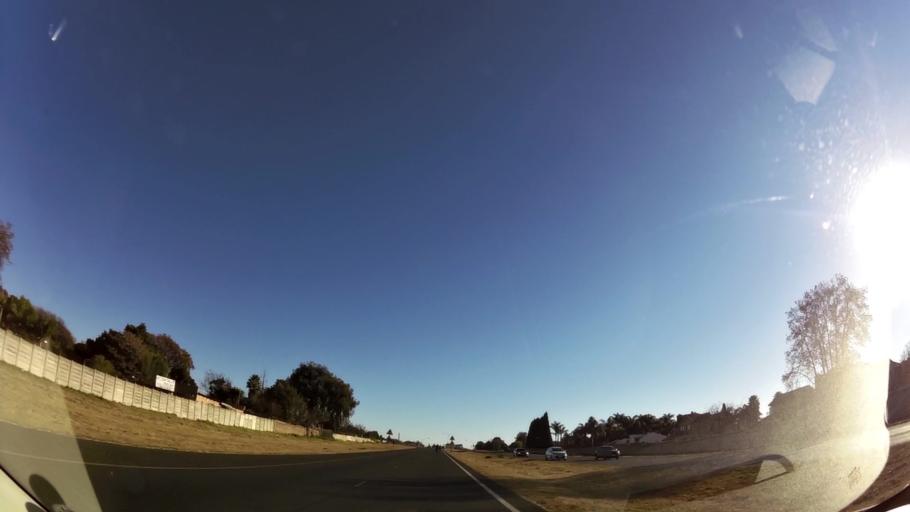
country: ZA
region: Gauteng
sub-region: City of Johannesburg Metropolitan Municipality
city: Modderfontein
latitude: -26.0811
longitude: 28.2044
